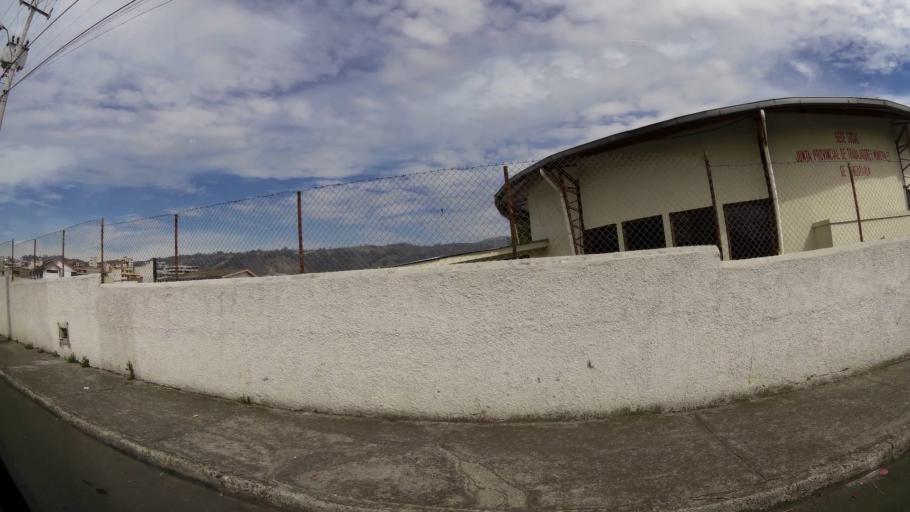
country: EC
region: Tungurahua
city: Ambato
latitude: -1.2532
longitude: -78.6324
